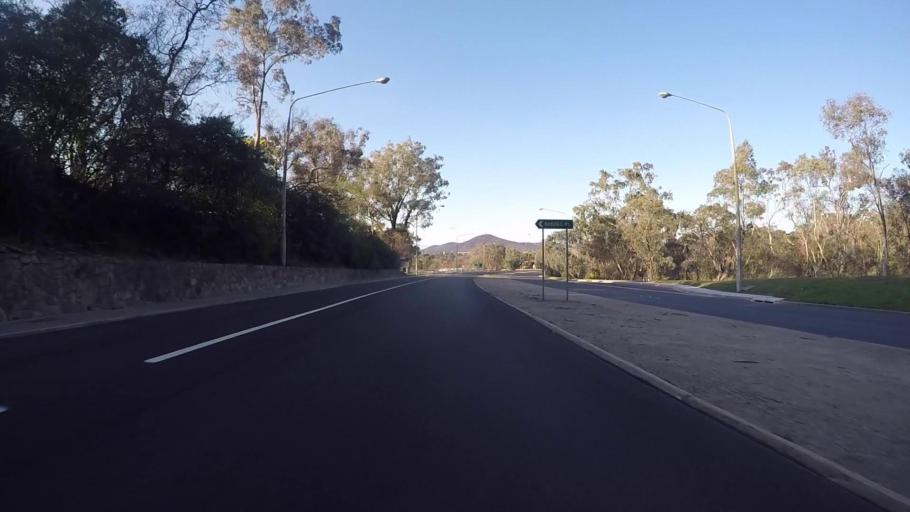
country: AU
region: Australian Capital Territory
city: Forrest
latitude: -35.3058
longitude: 149.1201
